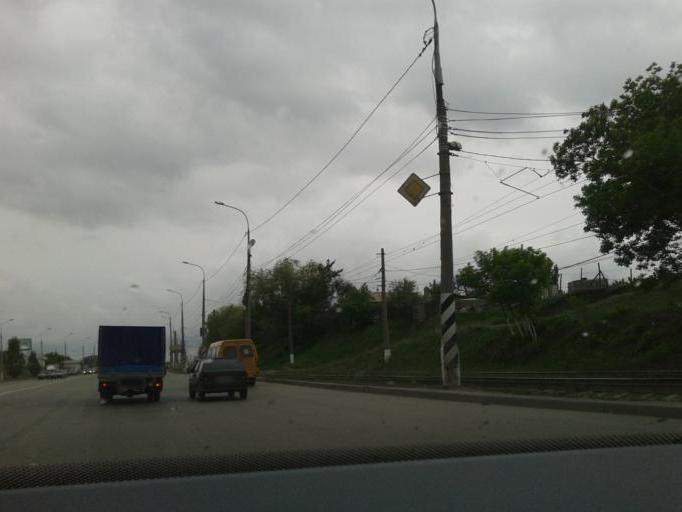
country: RU
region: Volgograd
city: Volgograd
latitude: 48.6882
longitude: 44.4558
